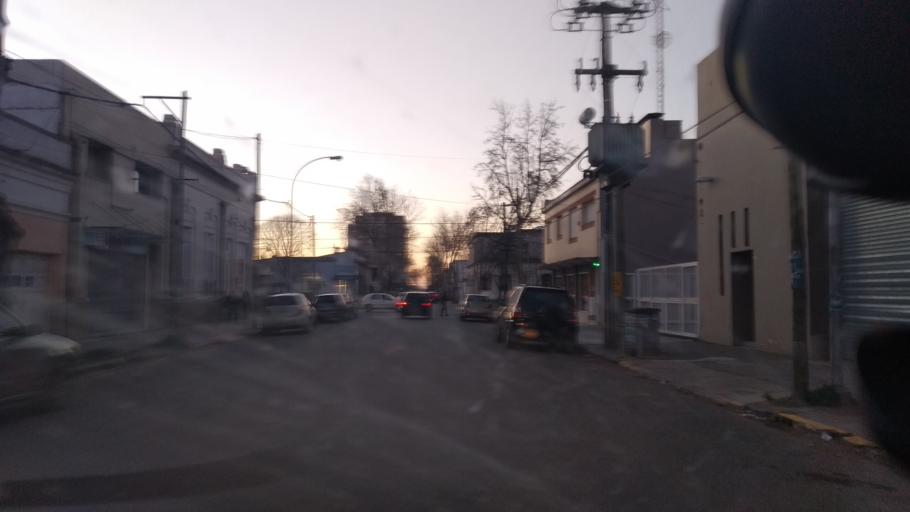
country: AR
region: Buenos Aires
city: Necochea
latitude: -38.5566
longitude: -58.7407
